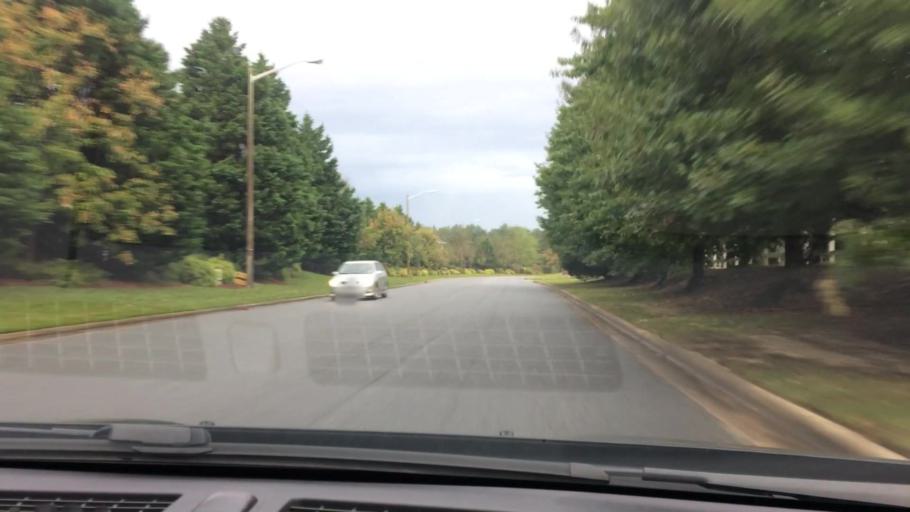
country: US
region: North Carolina
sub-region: Pitt County
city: Windsor
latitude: 35.5680
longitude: -77.3637
